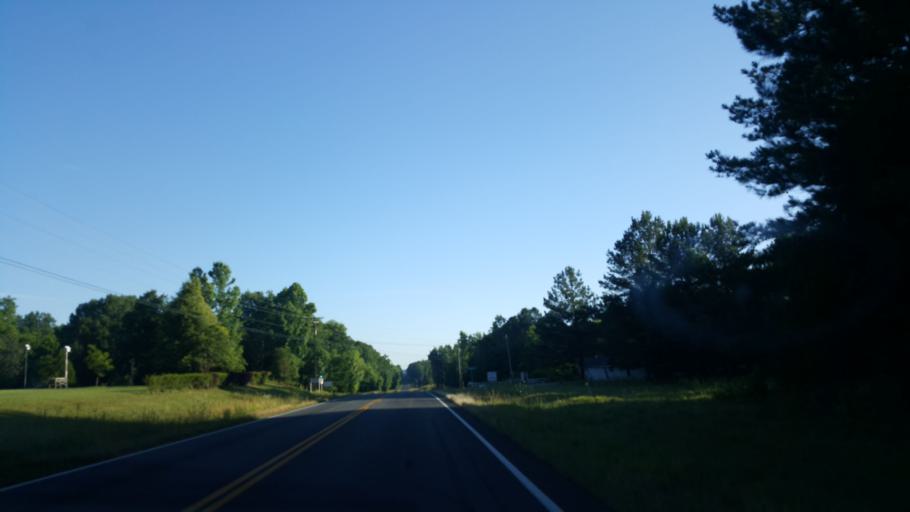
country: US
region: Tennessee
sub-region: Henderson County
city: Lexington
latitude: 35.5390
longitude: -88.3832
